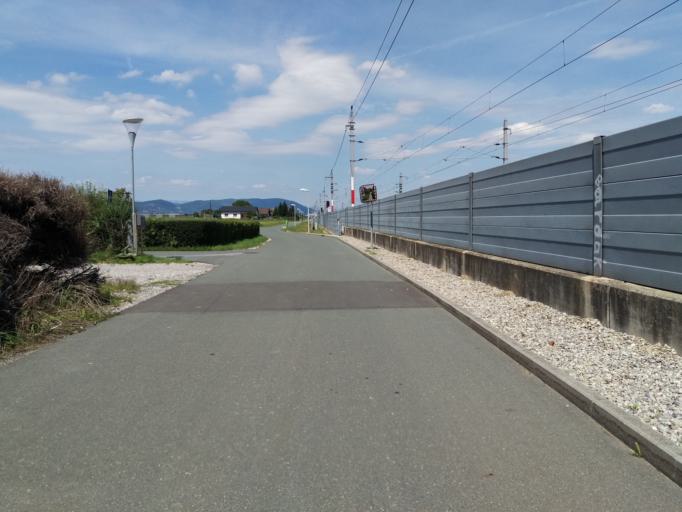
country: AT
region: Styria
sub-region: Politischer Bezirk Graz-Umgebung
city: Feldkirchen bei Graz
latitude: 46.9935
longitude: 15.4520
